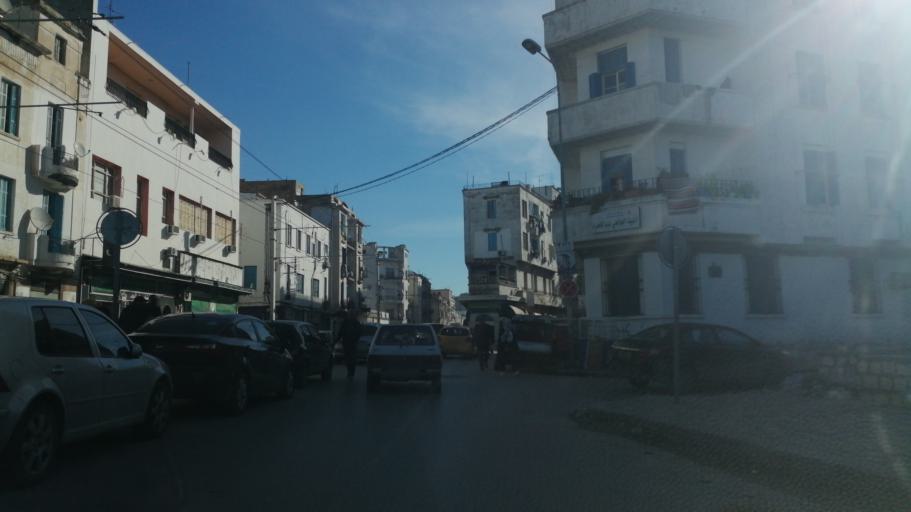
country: TN
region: Tunis
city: Tunis
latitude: 36.8095
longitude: 10.1742
